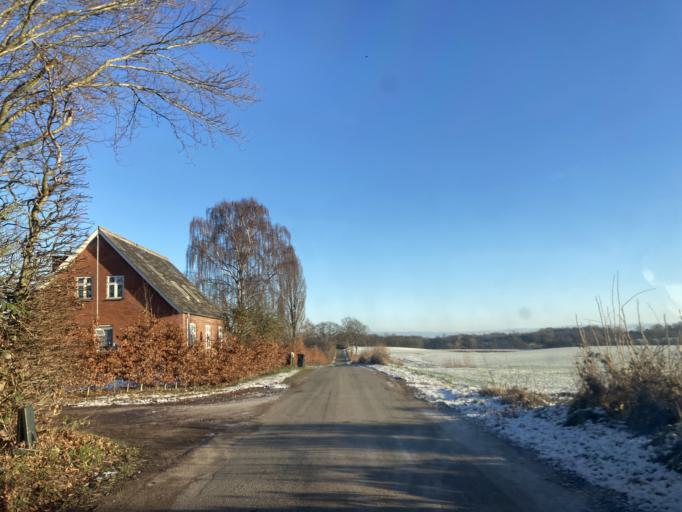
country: DK
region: South Denmark
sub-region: Svendborg Kommune
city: Thuro By
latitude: 55.1485
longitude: 10.7301
